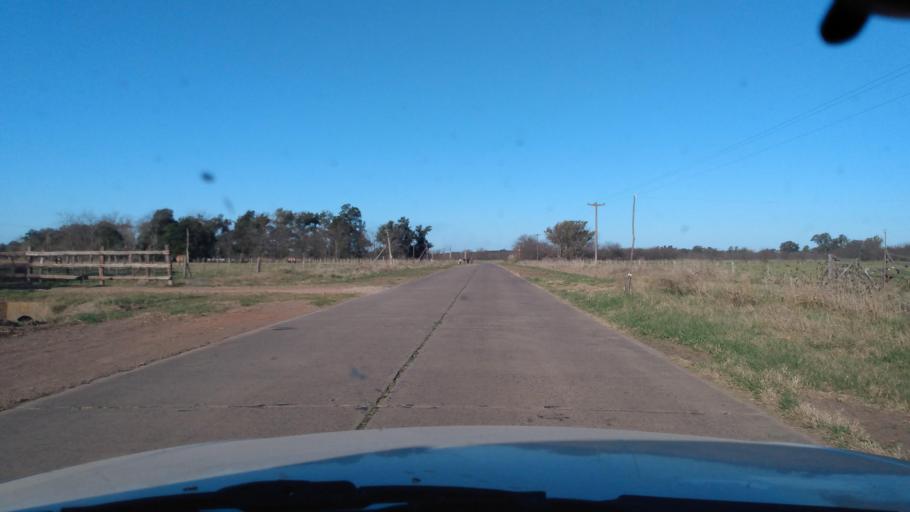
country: AR
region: Buenos Aires
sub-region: Partido de Mercedes
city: Mercedes
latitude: -34.6143
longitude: -59.2695
